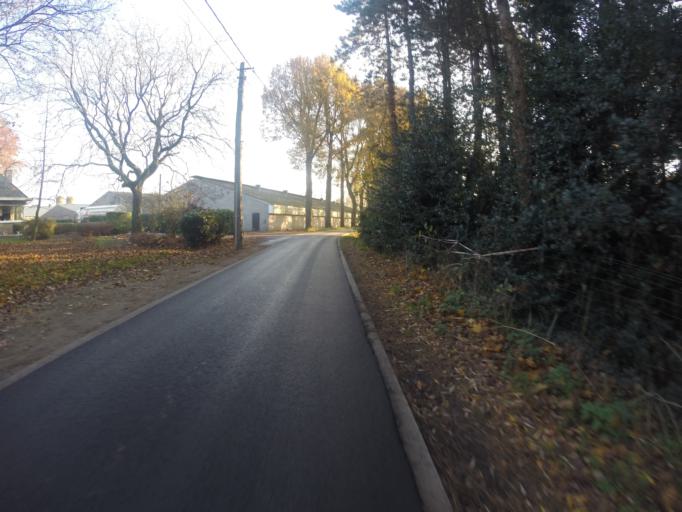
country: BE
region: Flanders
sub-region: Provincie Oost-Vlaanderen
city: Aalter
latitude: 51.0842
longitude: 3.4190
